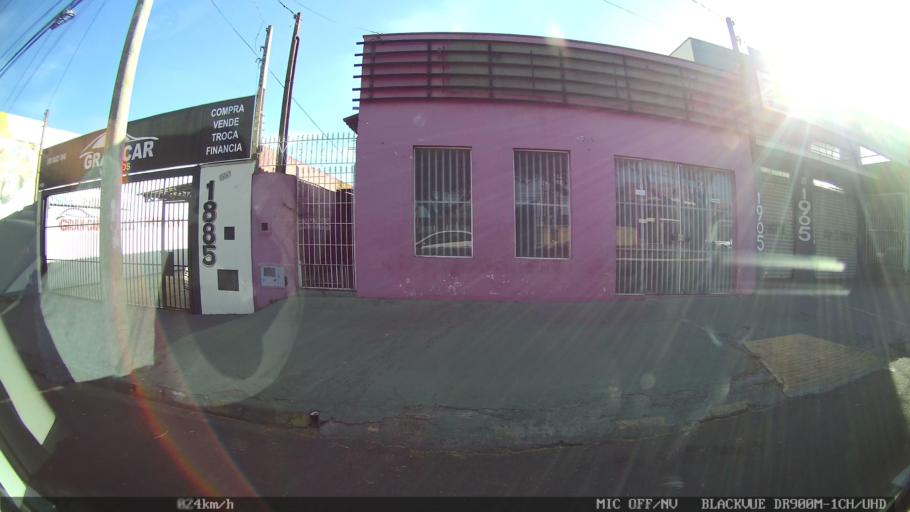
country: BR
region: Sao Paulo
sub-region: Franca
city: Franca
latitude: -20.5165
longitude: -47.3981
